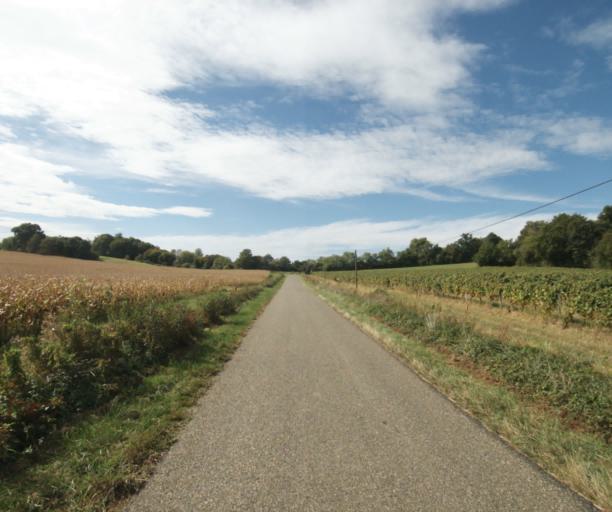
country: FR
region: Aquitaine
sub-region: Departement des Landes
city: Villeneuve-de-Marsan
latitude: 43.9003
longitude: -0.2123
